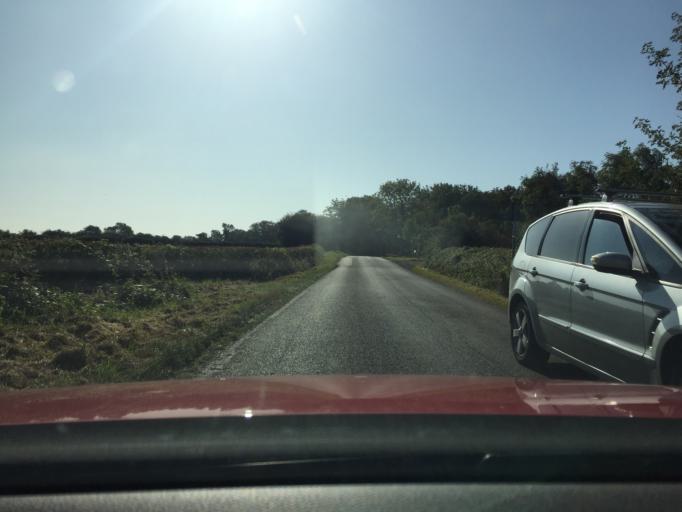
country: GB
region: England
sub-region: Leicestershire
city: Houghton on the Hill
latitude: 52.6560
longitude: -1.0146
